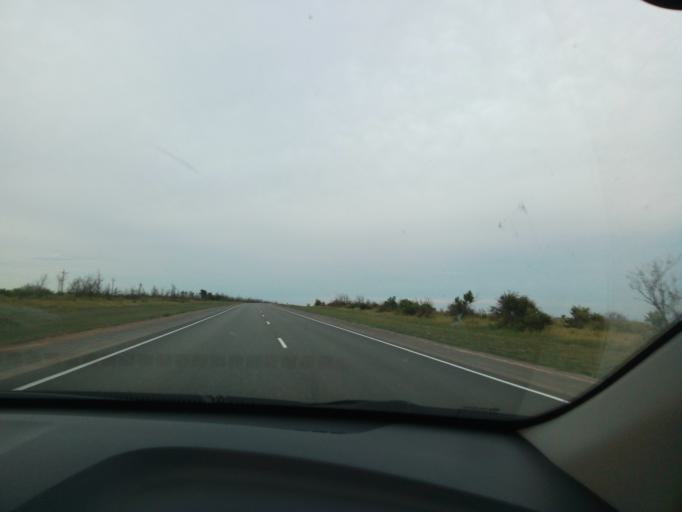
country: RU
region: Volgograd
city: Dubovka
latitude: 49.1533
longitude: 44.8402
